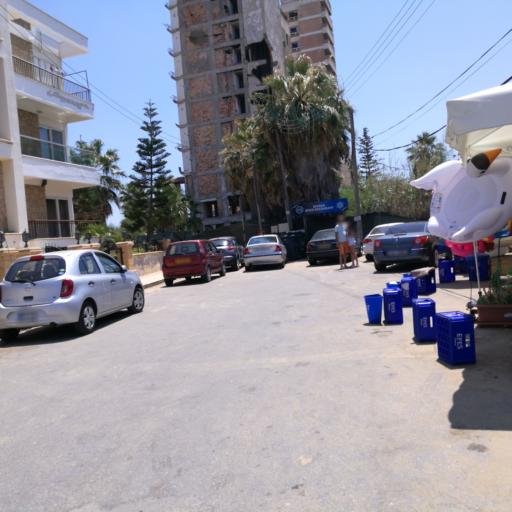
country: CY
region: Ammochostos
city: Famagusta
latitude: 35.1188
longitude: 33.9573
